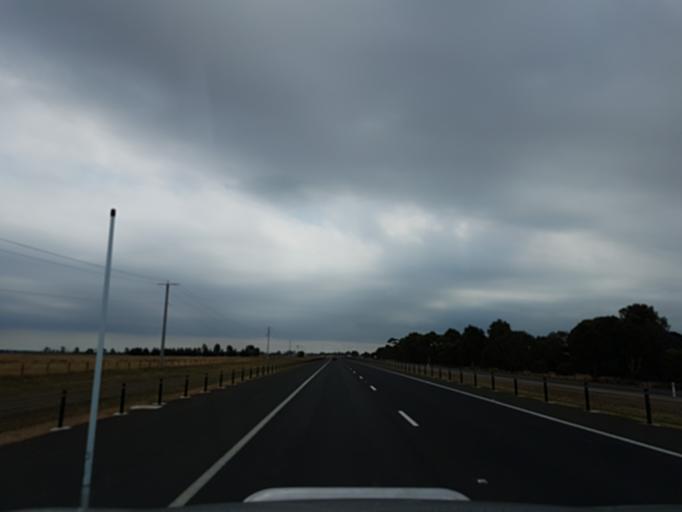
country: AU
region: Victoria
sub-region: Wellington
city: Sale
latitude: -38.1008
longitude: 146.9975
